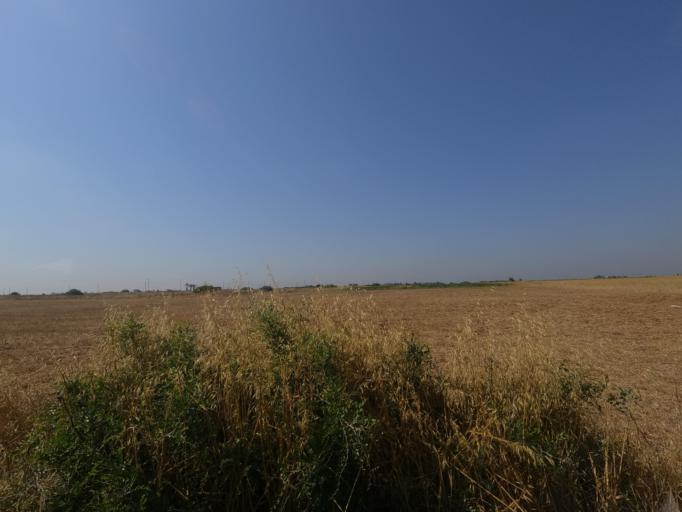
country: CY
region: Ammochostos
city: Avgorou
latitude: 35.0608
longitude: 33.8608
